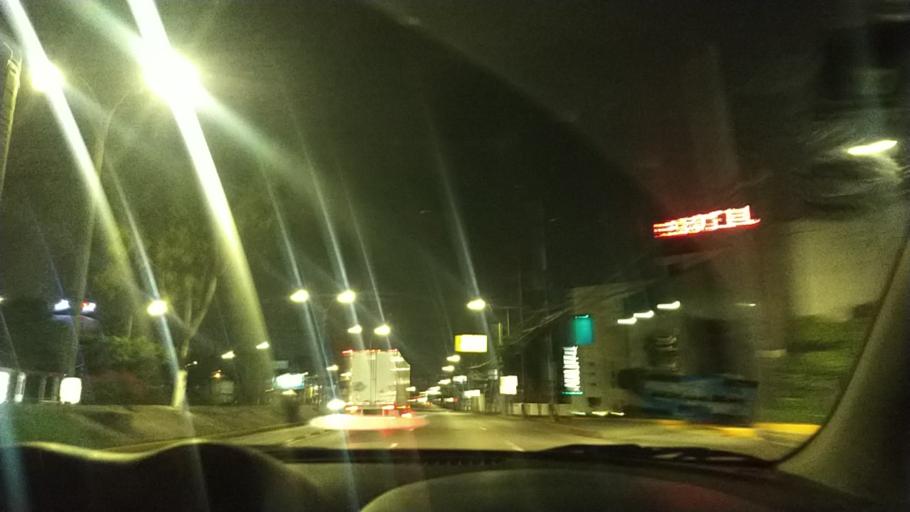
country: MX
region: Mexico
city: Coacalco
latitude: 19.6290
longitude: -99.0838
